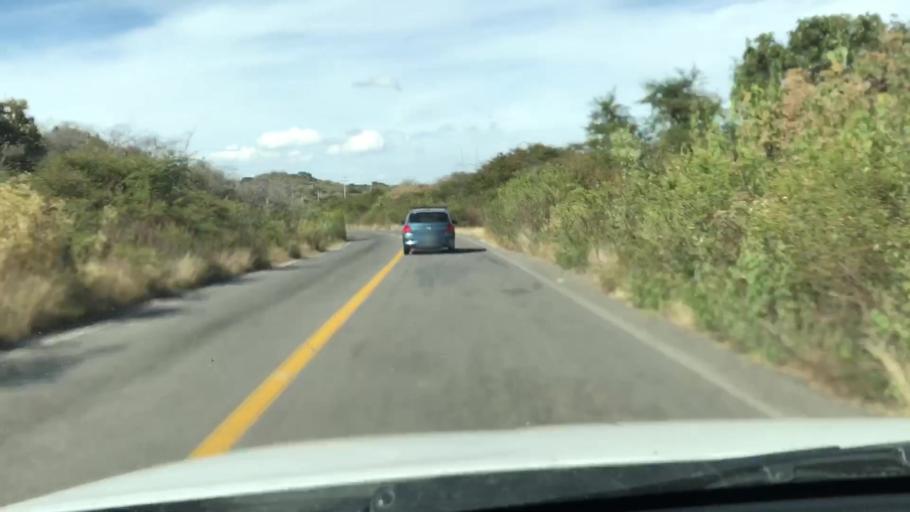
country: MX
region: Jalisco
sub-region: Zacoalco de Torres
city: Barranca de Otates (Barranca de Otatan)
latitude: 20.2077
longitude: -103.6926
